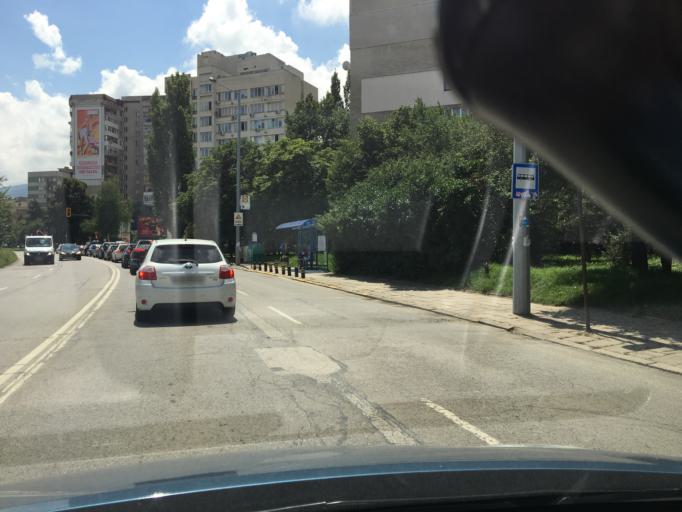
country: BG
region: Sofia-Capital
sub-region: Stolichna Obshtina
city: Sofia
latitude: 42.6645
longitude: 23.3027
